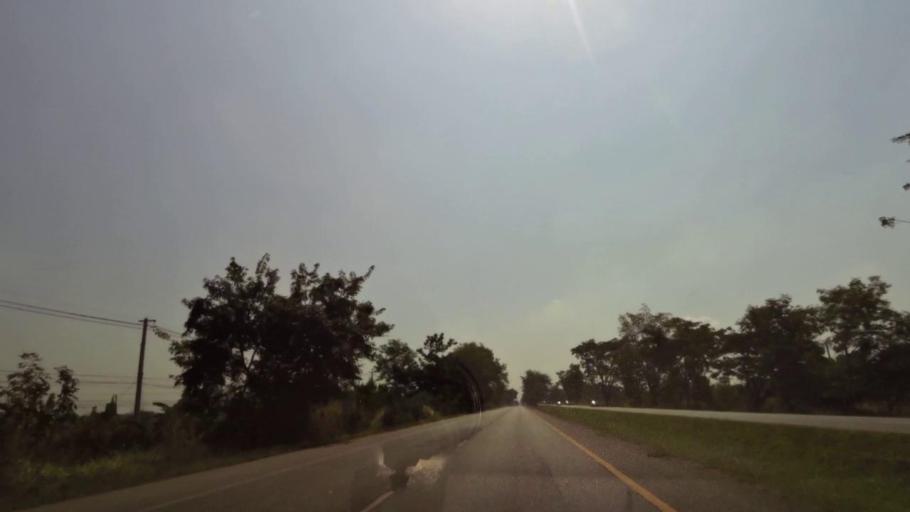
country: TH
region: Phichit
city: Bueng Na Rang
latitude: 16.2837
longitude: 100.1275
